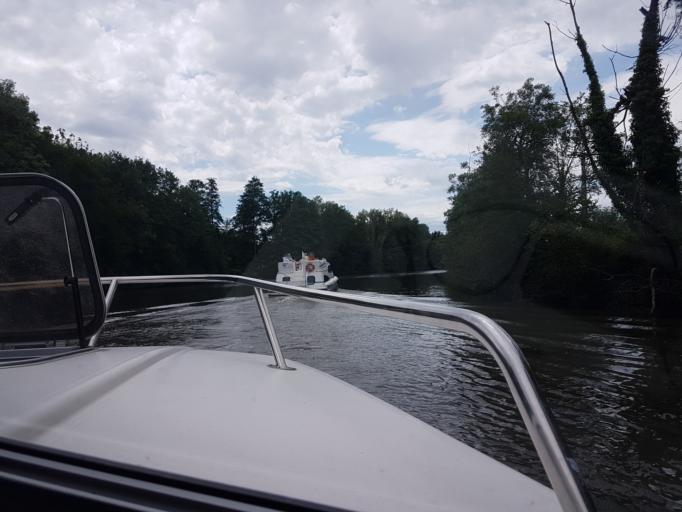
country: FR
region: Bourgogne
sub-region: Departement de la Nievre
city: Clamecy
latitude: 47.4660
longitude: 3.5278
